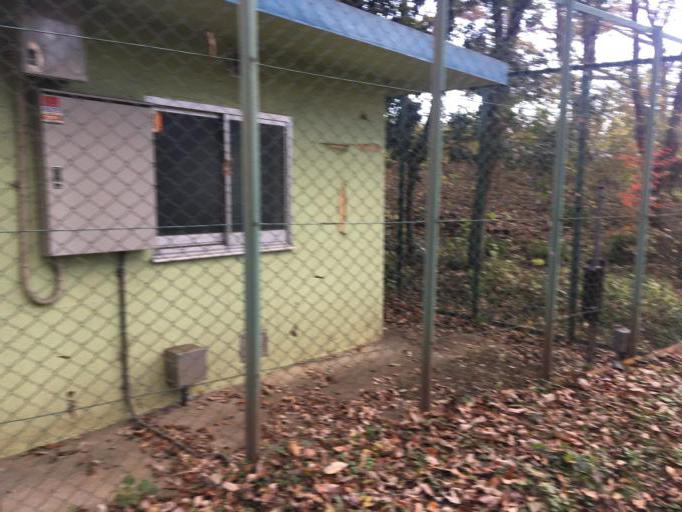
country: JP
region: Saitama
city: Ogawa
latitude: 36.0340
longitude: 139.3212
